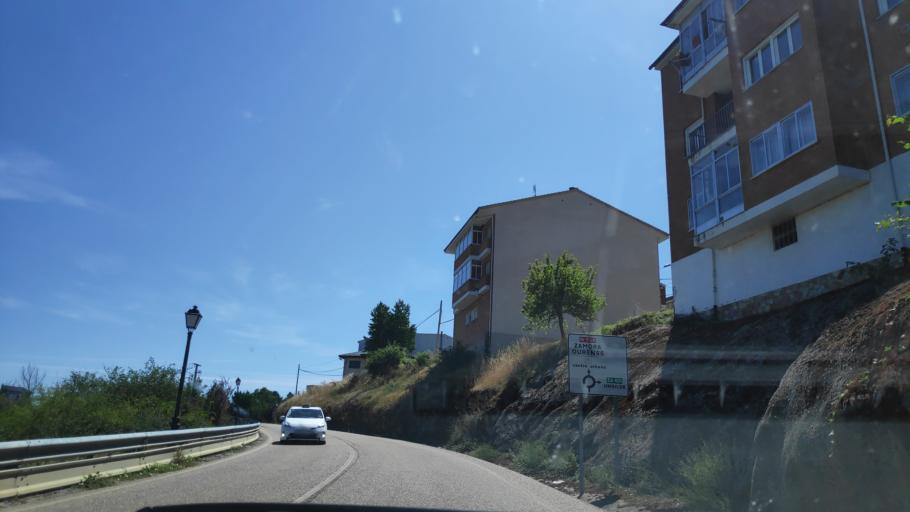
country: ES
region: Castille and Leon
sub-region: Provincia de Zamora
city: Puebla de Sanabria
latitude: 42.0518
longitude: -6.6374
